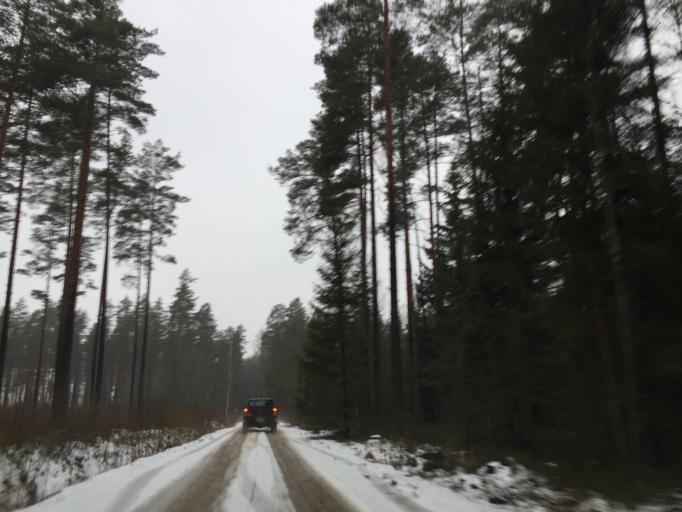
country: LV
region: Seja
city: Loja
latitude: 57.1306
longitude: 24.6016
